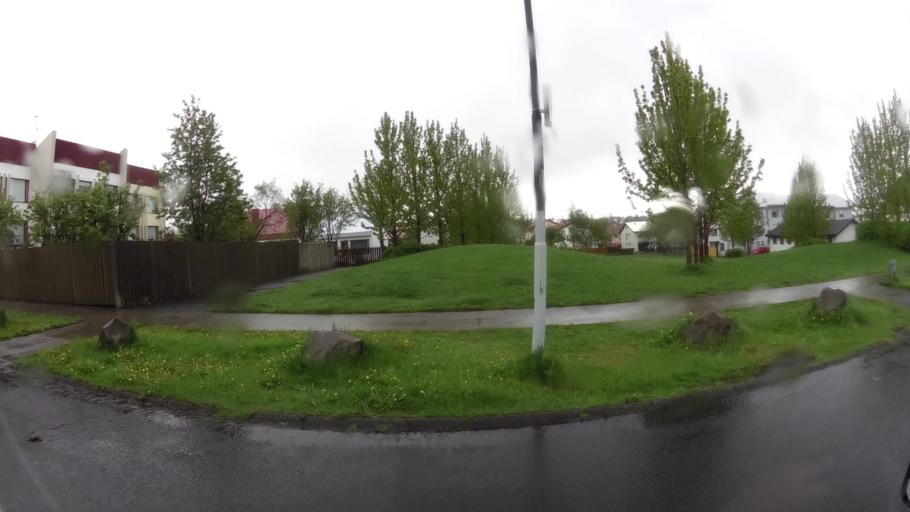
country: IS
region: Capital Region
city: Reykjavik
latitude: 64.0968
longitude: -21.8347
